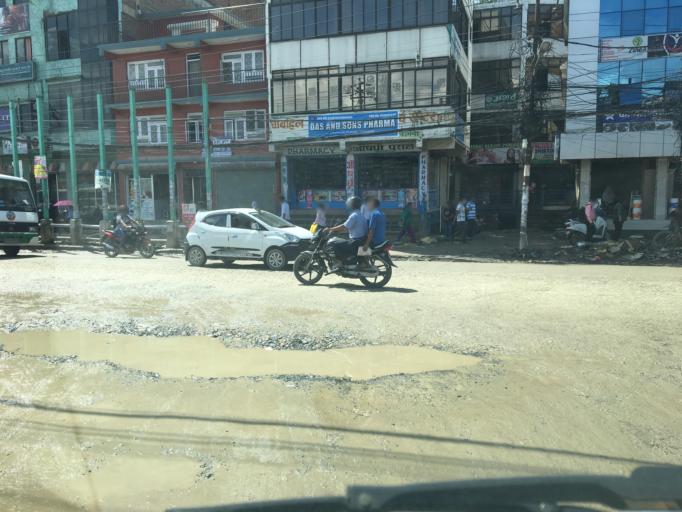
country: NP
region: Central Region
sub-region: Bagmati Zone
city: Kathmandu
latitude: 27.7194
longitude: 85.3509
